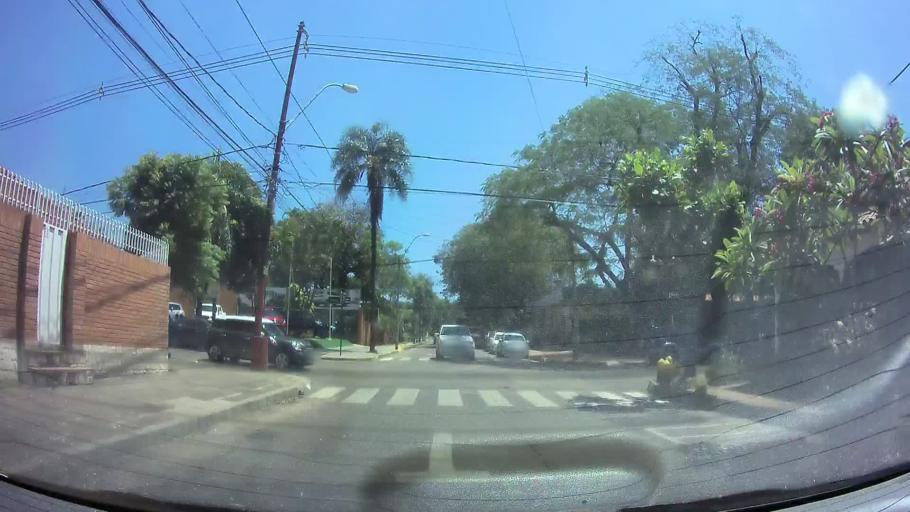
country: PY
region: Central
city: Lambare
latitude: -25.3020
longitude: -57.5824
